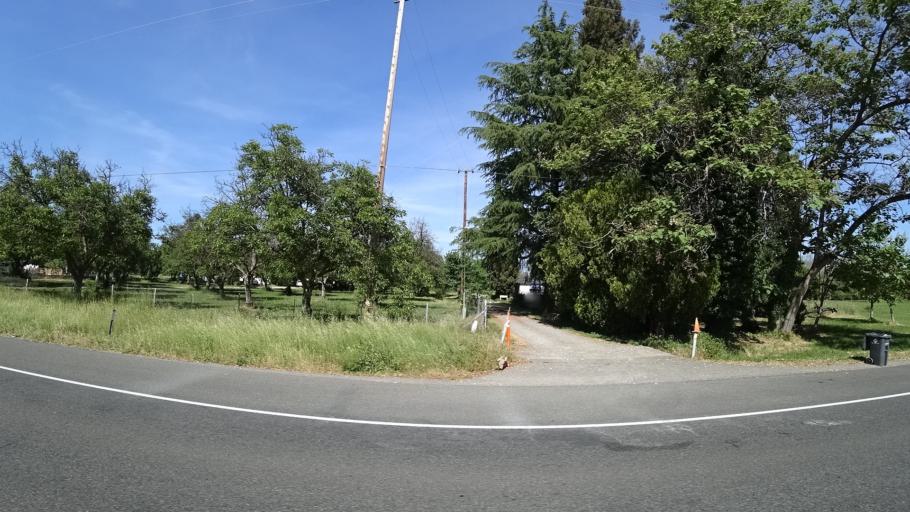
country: US
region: California
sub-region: Tehama County
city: Red Bluff
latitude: 40.1536
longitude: -122.1436
